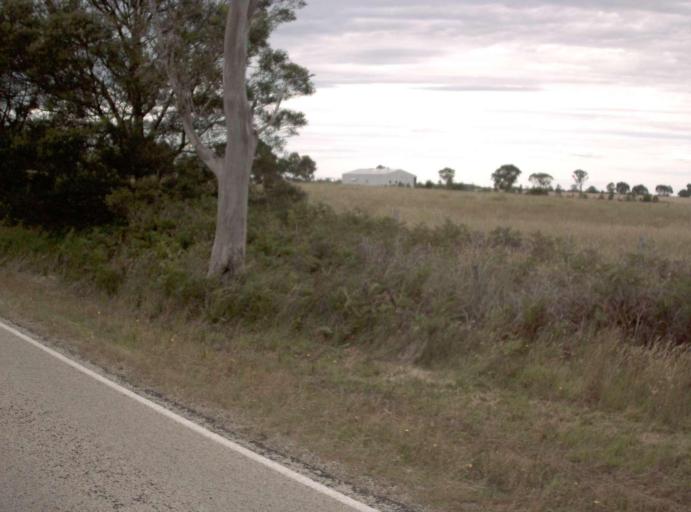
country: AU
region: Victoria
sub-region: East Gippsland
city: Bairnsdale
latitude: -37.9125
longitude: 147.5505
